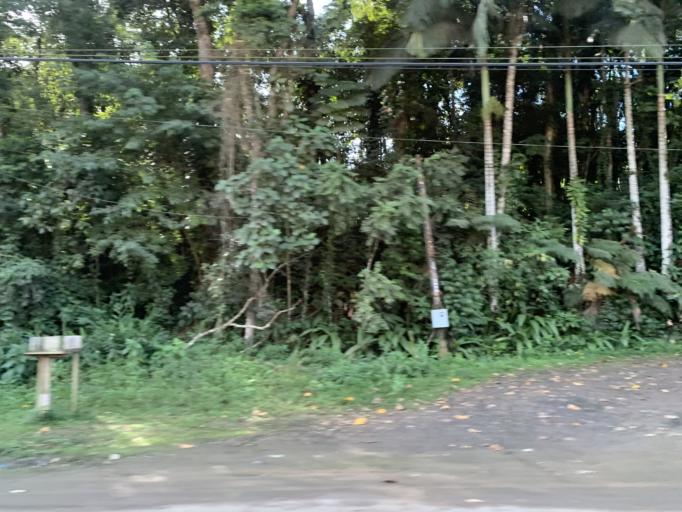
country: BR
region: Parana
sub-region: Antonina
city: Antonina
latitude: -25.4345
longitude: -48.7370
